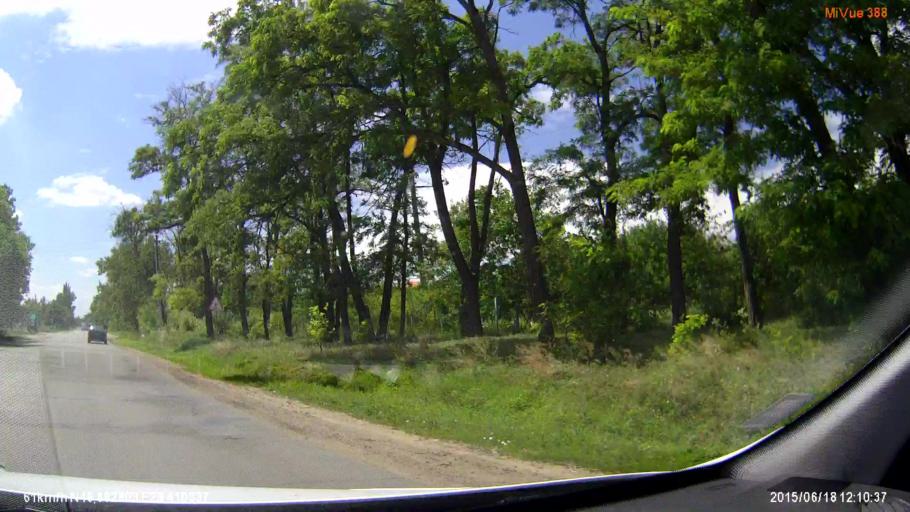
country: MD
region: Causeni
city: Causeni
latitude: 46.6626
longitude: 29.4102
